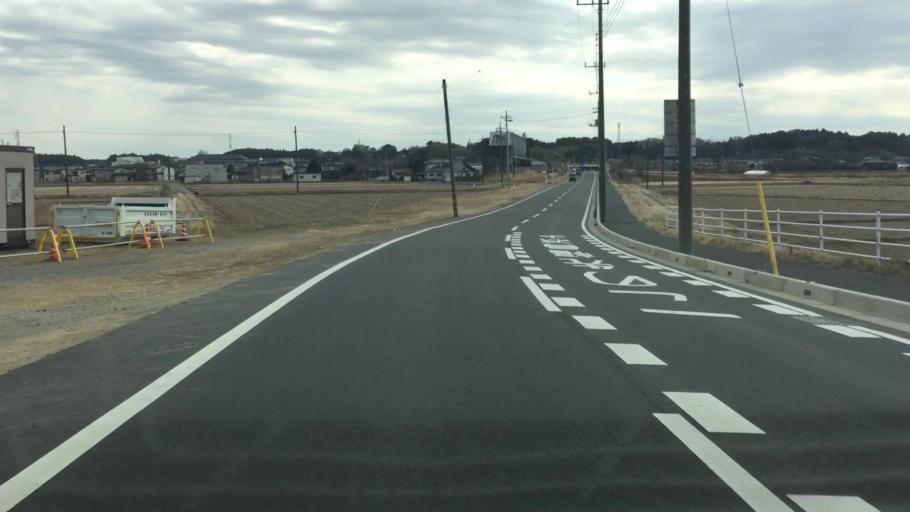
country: JP
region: Ibaraki
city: Ryugasaki
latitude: 35.8410
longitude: 140.1359
